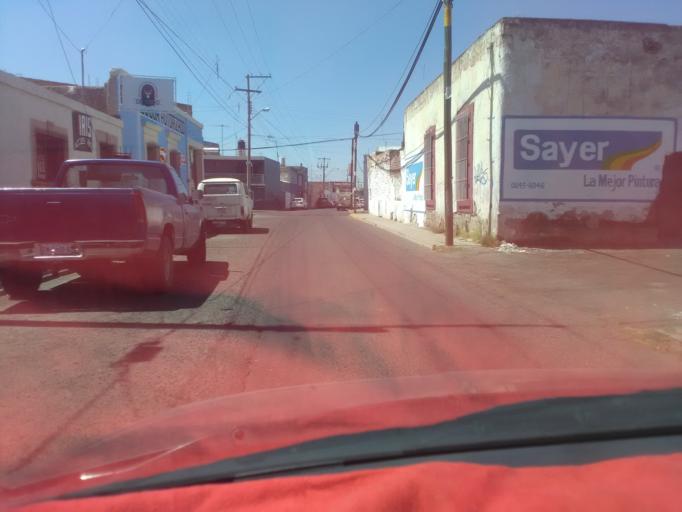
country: MX
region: Durango
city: Victoria de Durango
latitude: 24.0215
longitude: -104.6602
